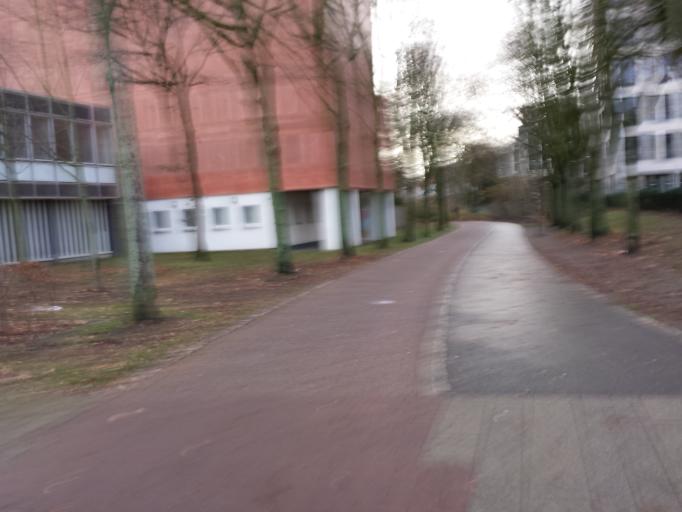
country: DE
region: Bremen
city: Bremen
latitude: 53.0768
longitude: 8.8157
